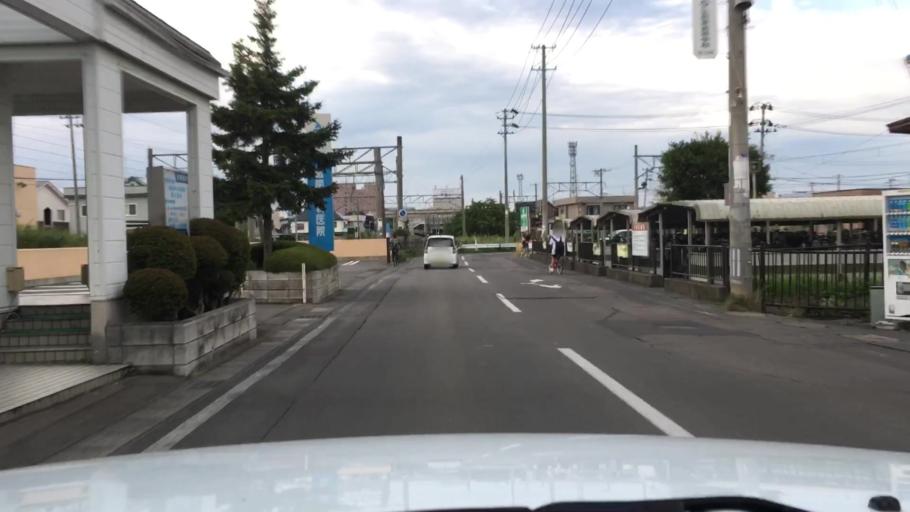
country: JP
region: Aomori
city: Hirosaki
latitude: 40.5922
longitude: 140.4880
